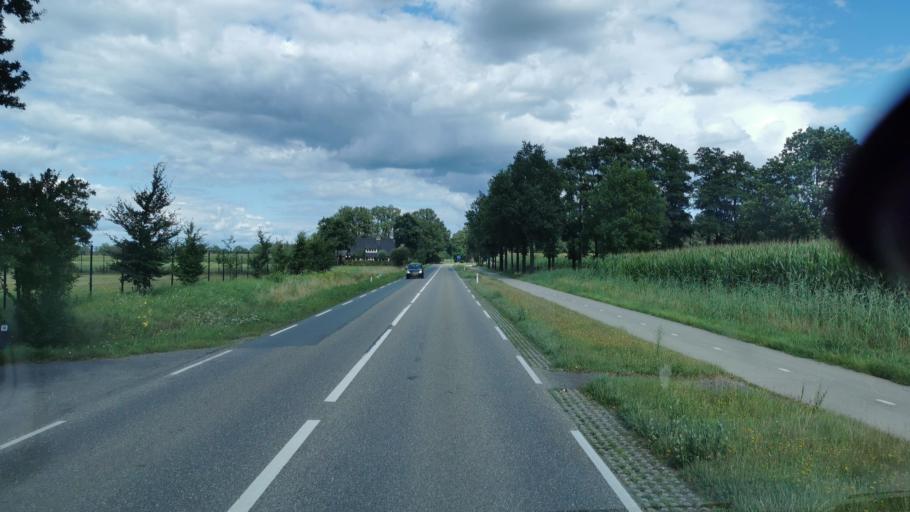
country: NL
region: Overijssel
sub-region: Gemeente Losser
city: Losser
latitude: 52.2313
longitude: 6.9898
